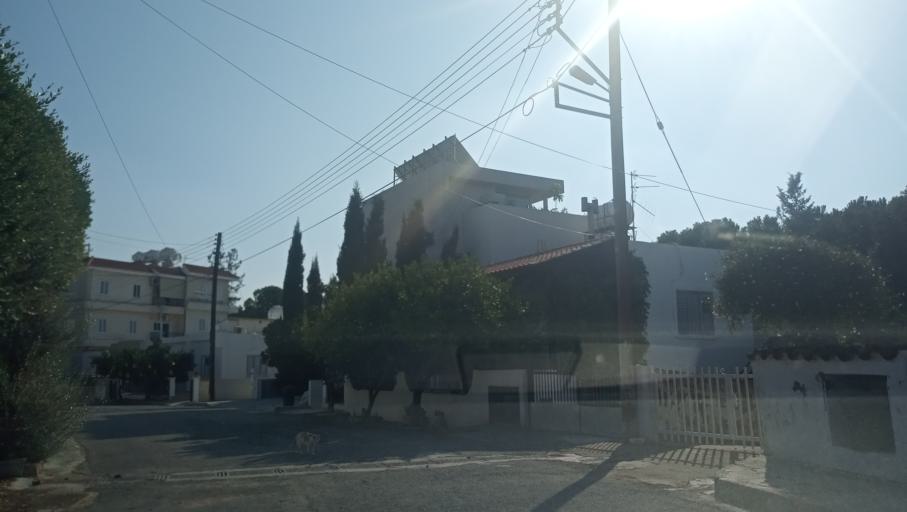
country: CY
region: Lefkosia
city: Nicosia
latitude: 35.1430
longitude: 33.3917
